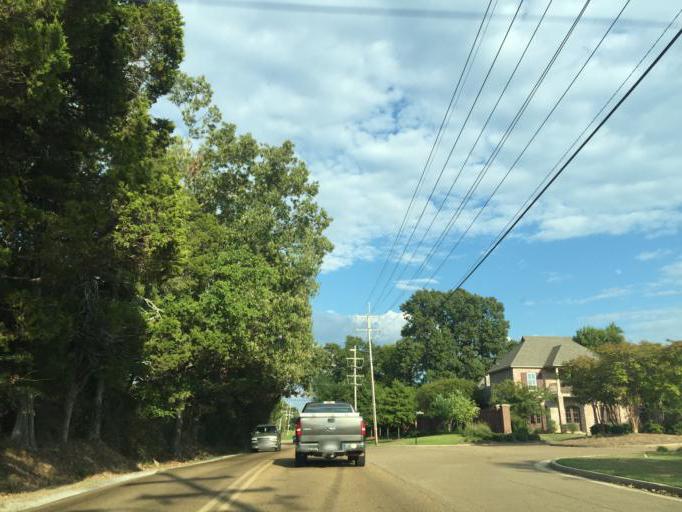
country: US
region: Mississippi
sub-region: Madison County
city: Madison
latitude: 32.4650
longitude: -90.1034
